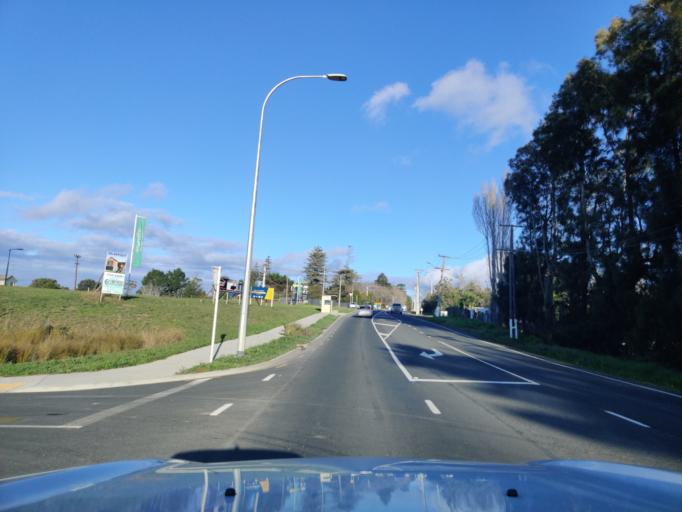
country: NZ
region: Auckland
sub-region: Auckland
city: Pakuranga
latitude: -36.9492
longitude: 174.9655
